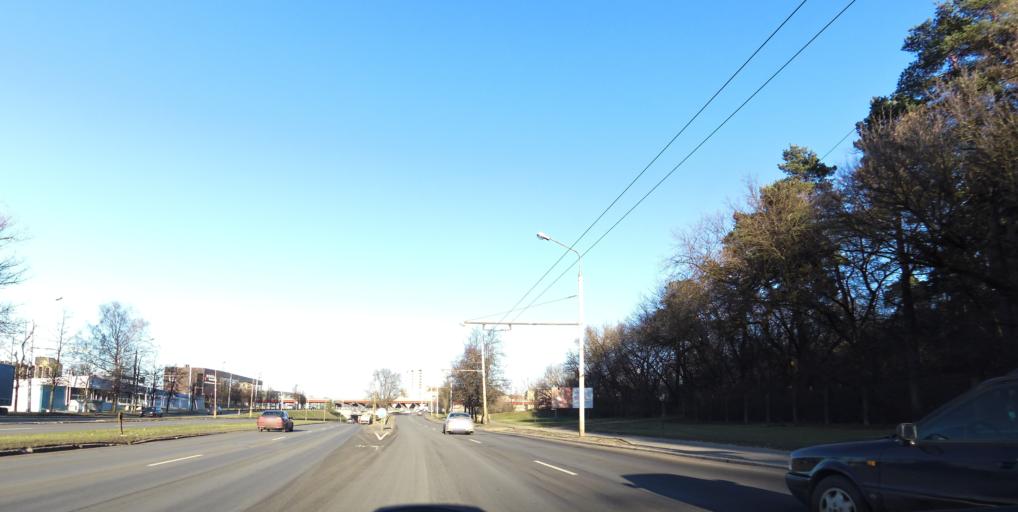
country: LT
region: Vilnius County
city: Vilkpede
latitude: 54.6658
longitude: 25.2372
